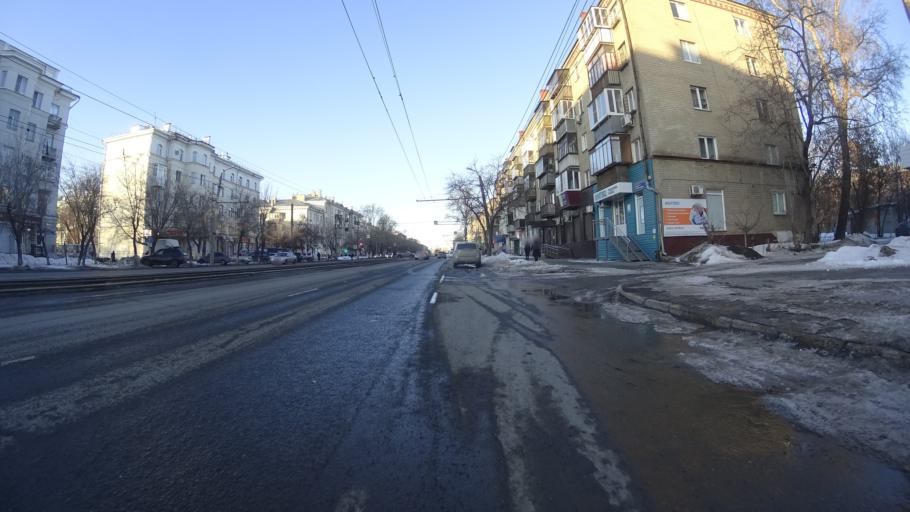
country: RU
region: Chelyabinsk
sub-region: Gorod Chelyabinsk
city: Chelyabinsk
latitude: 55.1406
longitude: 61.4420
